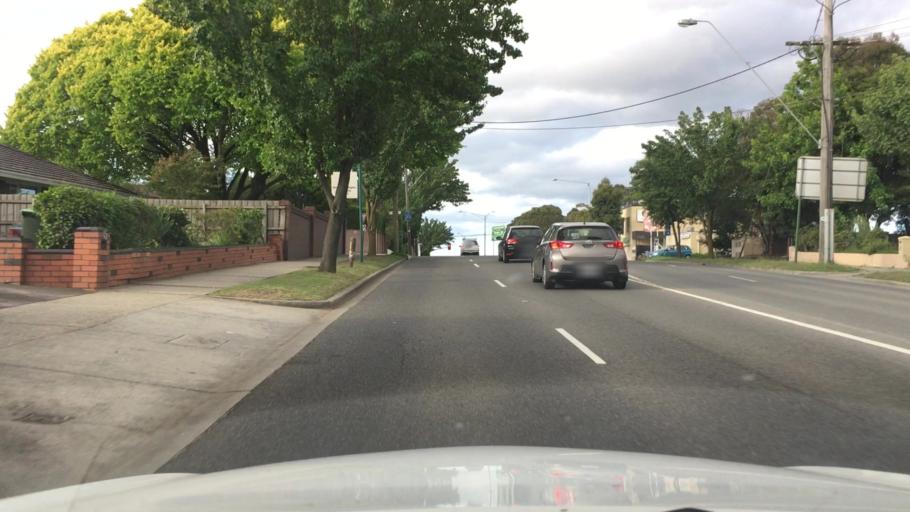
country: AU
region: Victoria
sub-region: Whitehorse
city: Burwood
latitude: -37.8536
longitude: 145.1321
